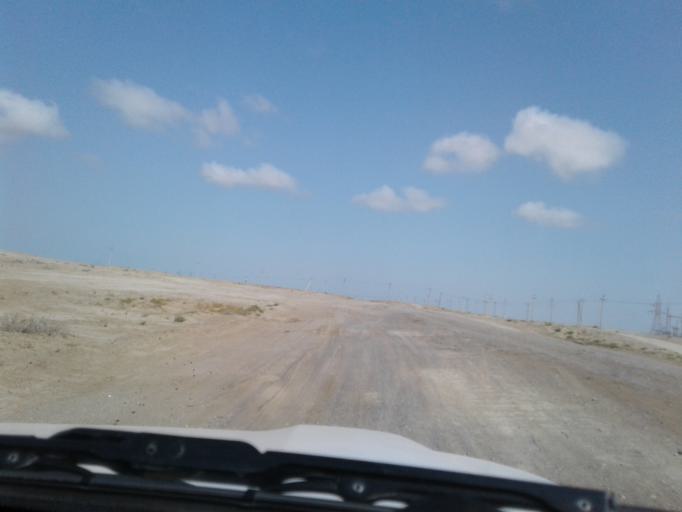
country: IR
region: Golestan
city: Gomishan
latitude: 37.7205
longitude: 53.9401
